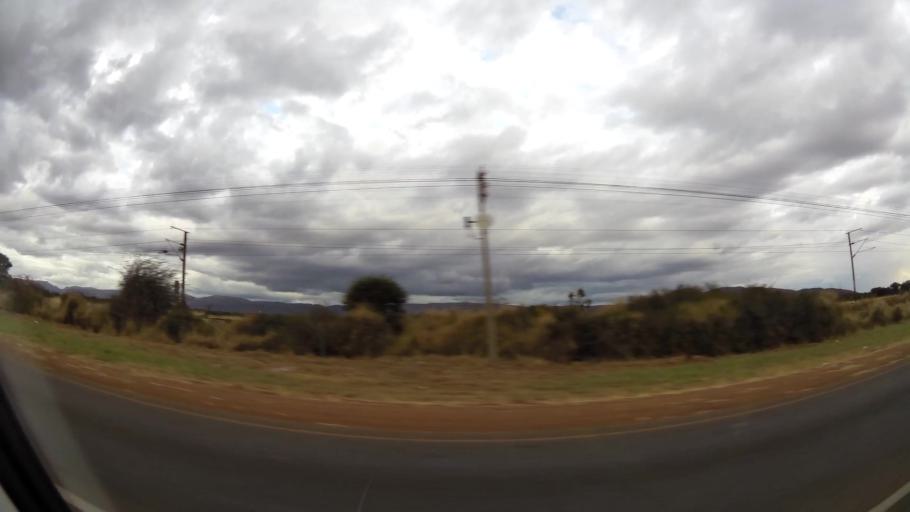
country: ZA
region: Limpopo
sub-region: Waterberg District Municipality
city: Mokopane
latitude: -24.2654
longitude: 28.9837
